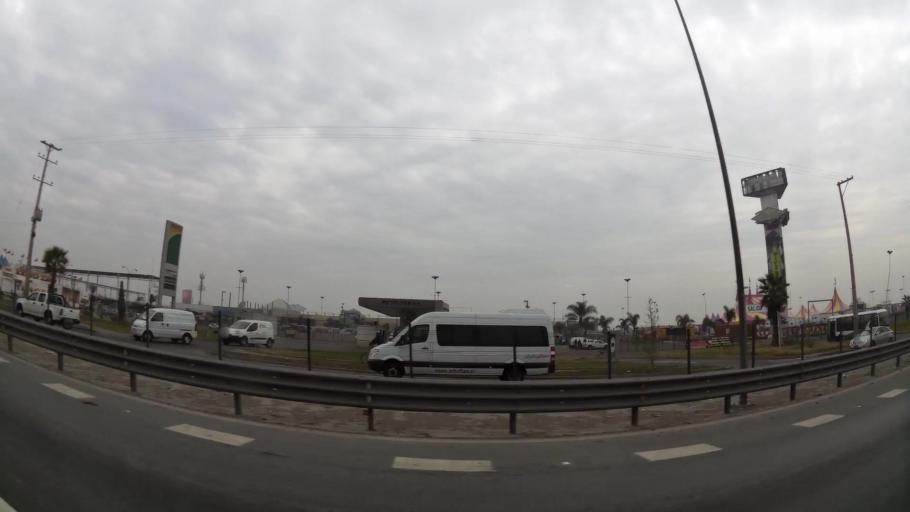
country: CL
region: Santiago Metropolitan
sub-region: Provincia de Maipo
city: San Bernardo
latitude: -33.5191
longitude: -70.7069
